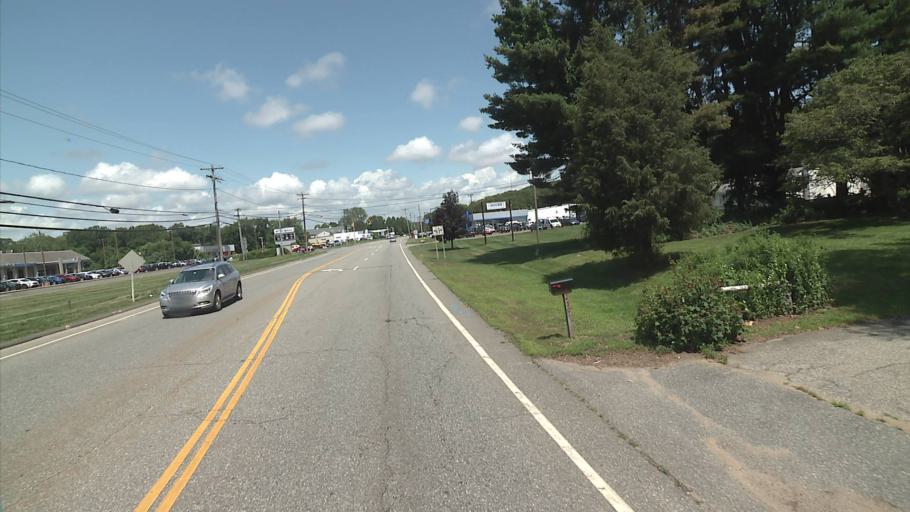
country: US
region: Connecticut
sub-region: Middlesex County
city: Old Saybrook
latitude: 41.3078
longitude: -72.3813
